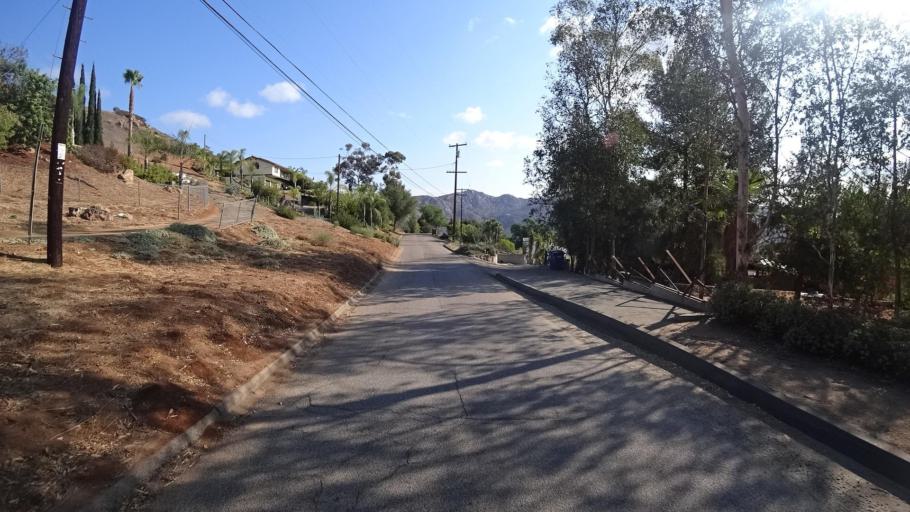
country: US
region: California
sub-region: San Diego County
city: Eucalyptus Hills
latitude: 32.8880
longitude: -116.9404
